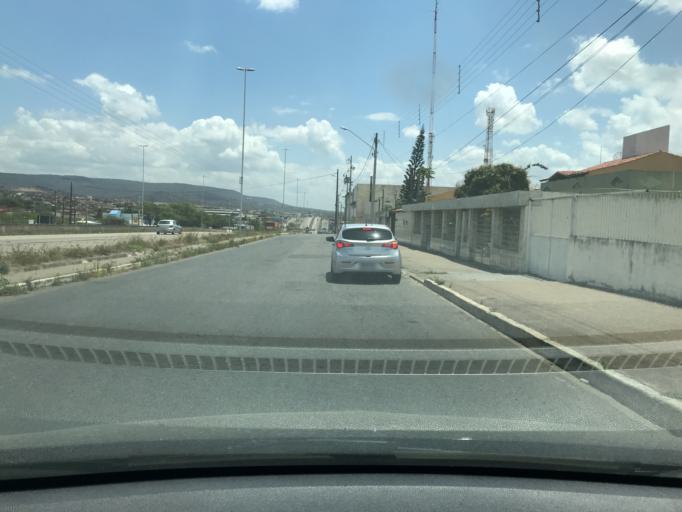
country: BR
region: Pernambuco
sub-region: Bezerros
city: Bezerros
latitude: -8.2416
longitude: -35.7508
